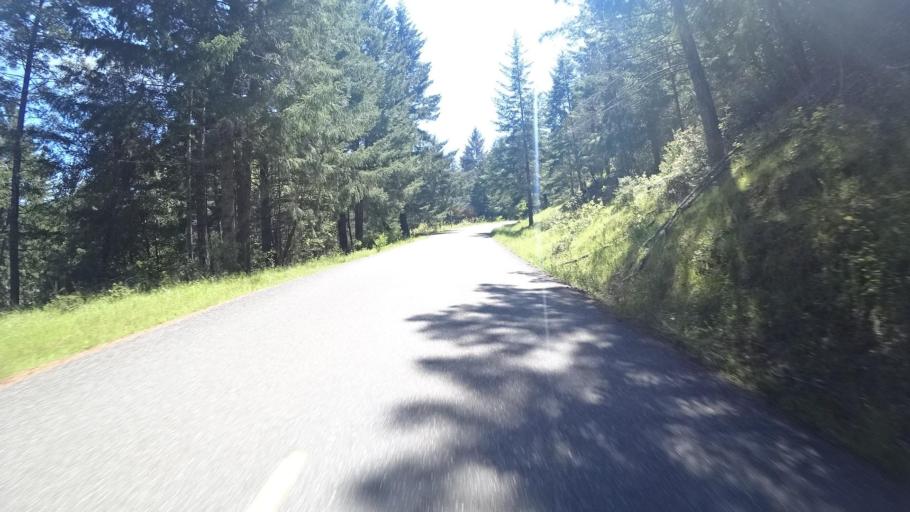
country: US
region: California
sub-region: Humboldt County
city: Rio Dell
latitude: 40.3279
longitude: -124.0439
